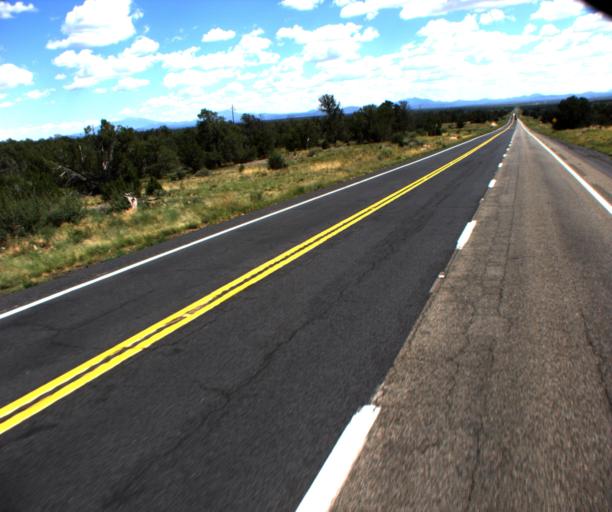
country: US
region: Arizona
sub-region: Coconino County
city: Grand Canyon Village
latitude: 35.8184
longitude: -112.1321
